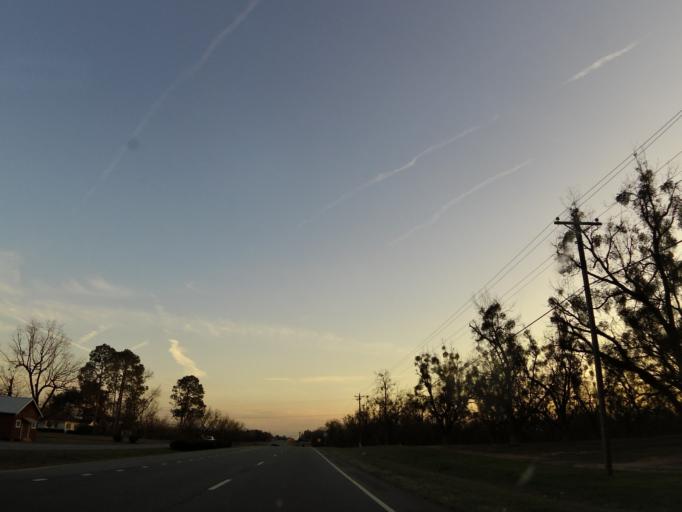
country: US
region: Georgia
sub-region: Lee County
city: Leesburg
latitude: 31.6869
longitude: -84.1729
